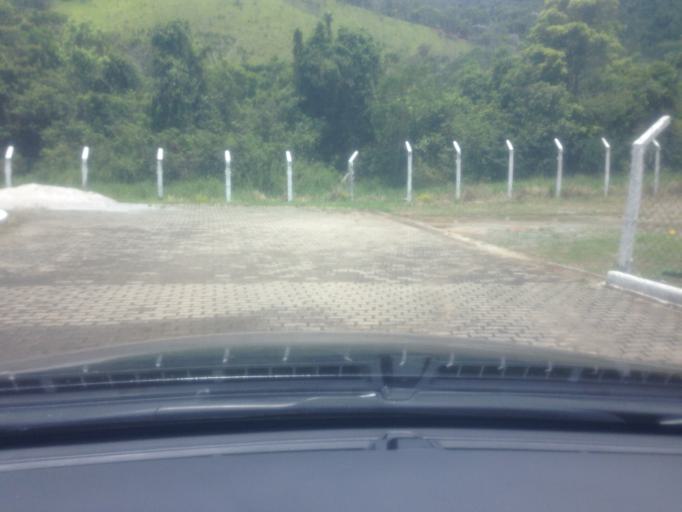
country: BR
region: Espirito Santo
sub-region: Guarapari
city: Guarapari
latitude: -20.5852
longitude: -40.5395
